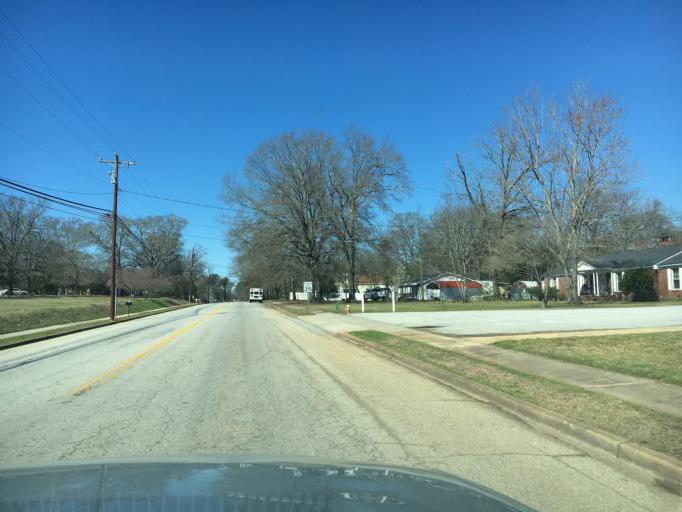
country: US
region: South Carolina
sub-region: Greenwood County
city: Ninety Six
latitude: 34.3062
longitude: -81.9848
